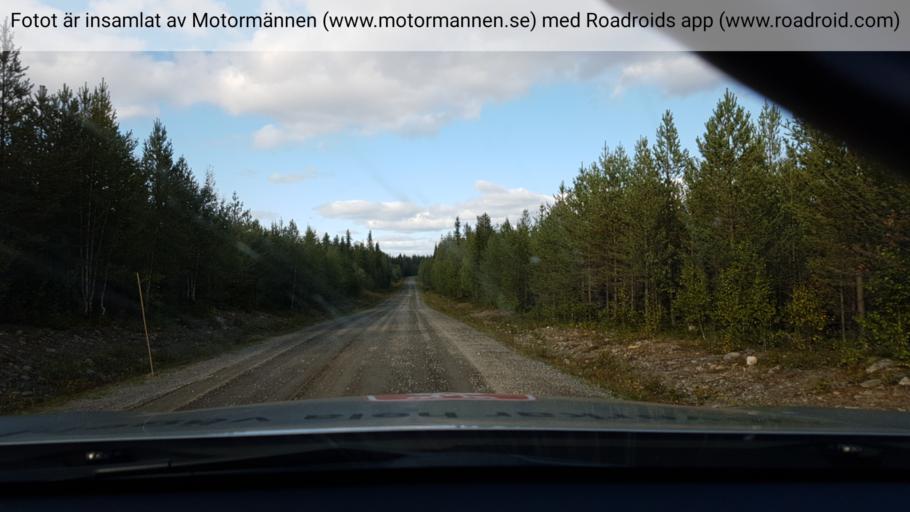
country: SE
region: Vaesterbotten
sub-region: Sorsele Kommun
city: Sorsele
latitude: 65.3956
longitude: 18.0778
